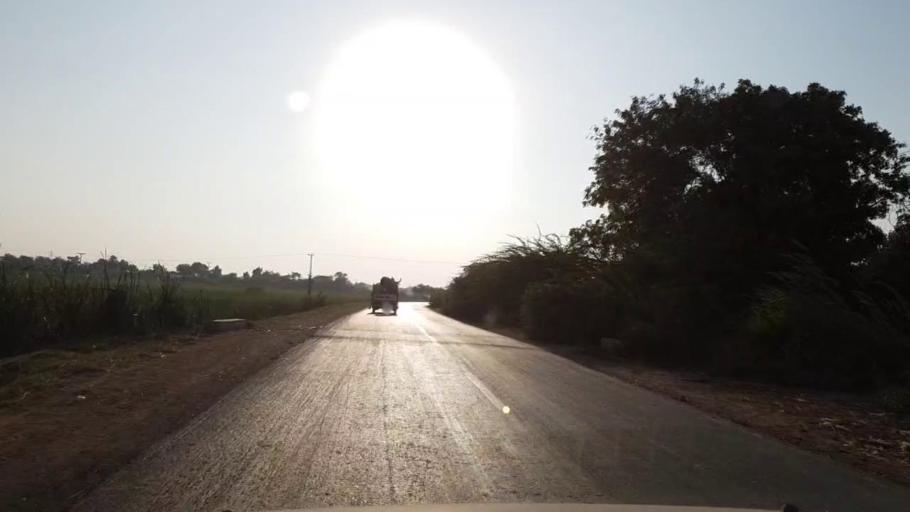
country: PK
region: Sindh
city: Mirpur Batoro
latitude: 24.6923
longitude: 68.1874
